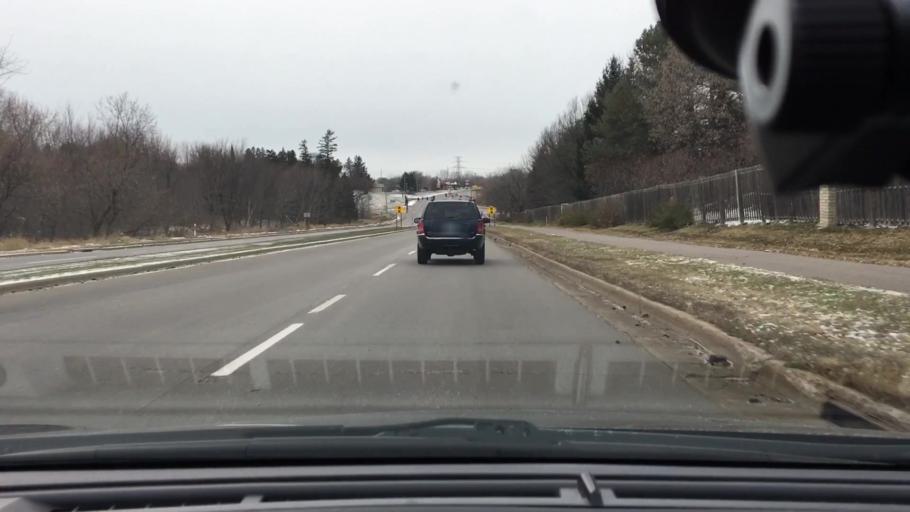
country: US
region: Minnesota
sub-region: Hennepin County
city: Plymouth
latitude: 45.0306
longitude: -93.4408
